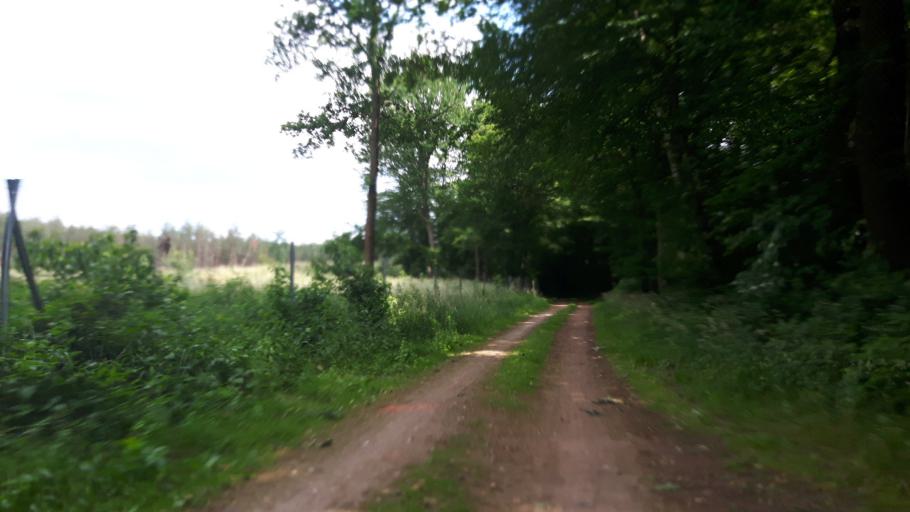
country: DE
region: Saxony-Anhalt
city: Radis
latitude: 51.7534
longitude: 12.4886
